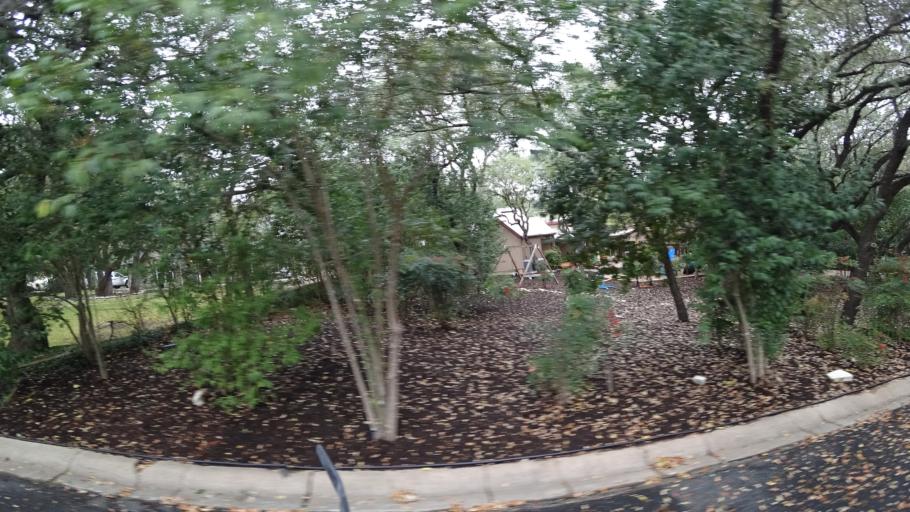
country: US
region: Texas
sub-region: Williamson County
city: Jollyville
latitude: 30.3787
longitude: -97.7858
